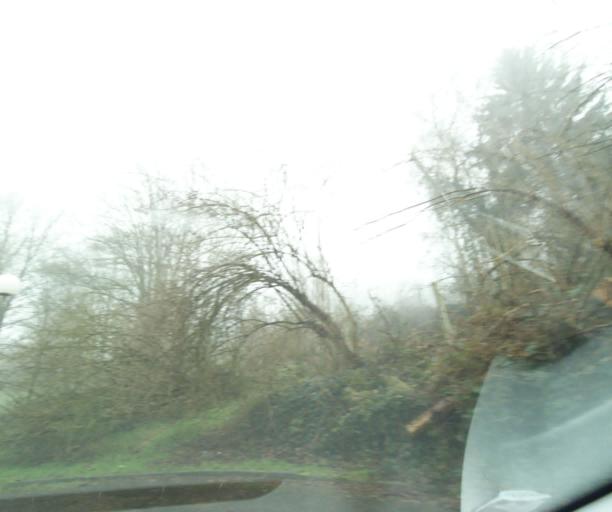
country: FR
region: Ile-de-France
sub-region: Departement de Seine-et-Marne
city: Dammartin-en-Goele
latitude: 49.0552
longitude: 2.6890
